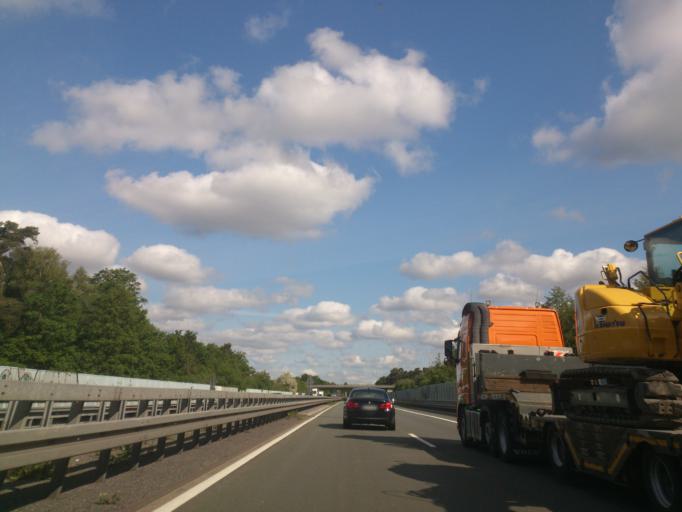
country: DE
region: North Rhine-Westphalia
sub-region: Regierungsbezirk Detmold
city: Hovelhof
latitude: 51.8679
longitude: 8.6569
